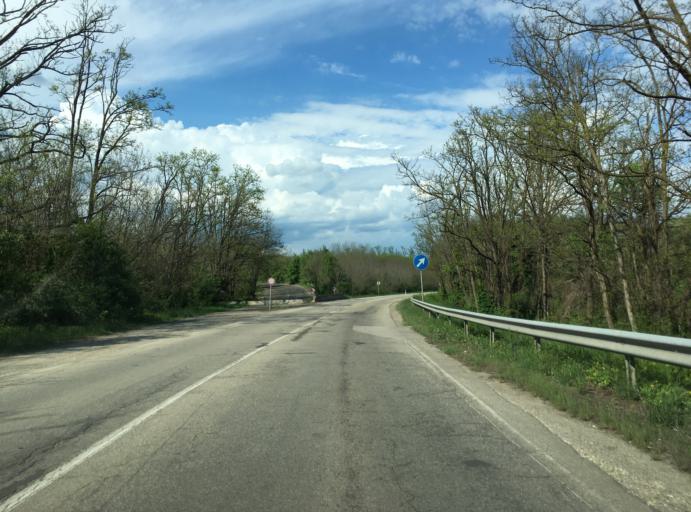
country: HU
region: Pest
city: Domony
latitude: 47.6164
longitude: 19.4075
